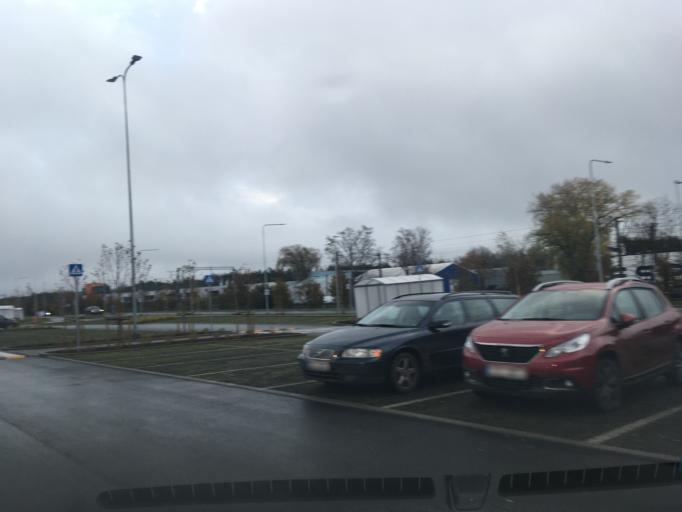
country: EE
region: Harju
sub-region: Tallinna linn
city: Tallinn
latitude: 59.4186
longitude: 24.7588
